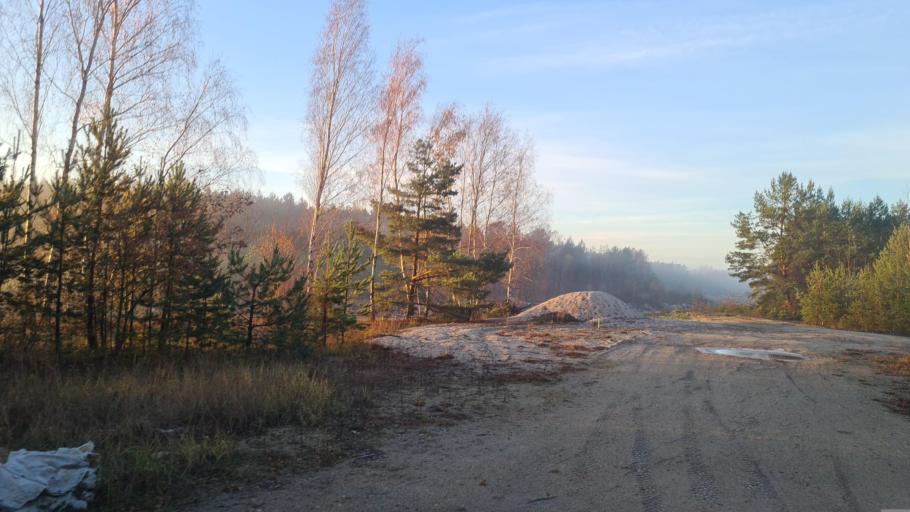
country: DE
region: Brandenburg
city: Lauchhammer
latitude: 51.5323
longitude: 13.7595
